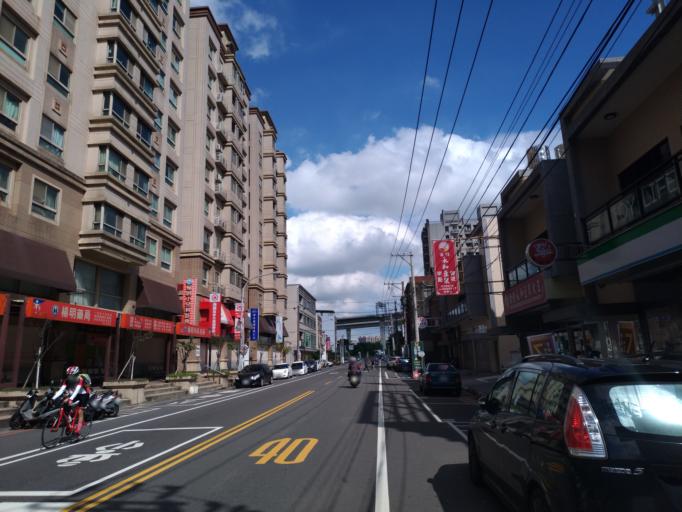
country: TW
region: Taiwan
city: Daxi
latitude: 24.9130
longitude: 121.1623
